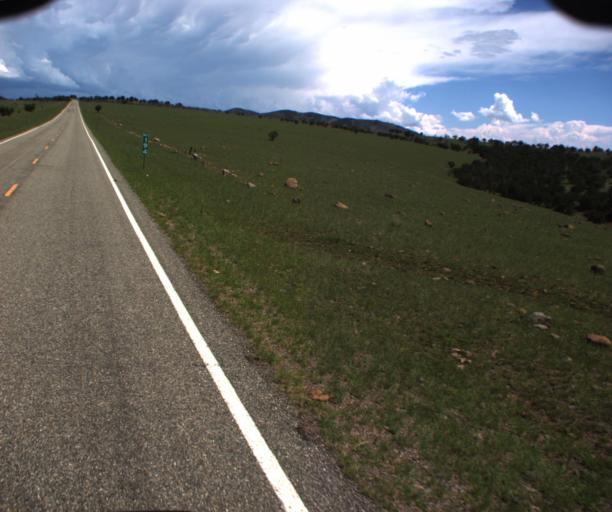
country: US
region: Arizona
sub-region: Greenlee County
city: Morenci
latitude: 33.3309
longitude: -109.3496
